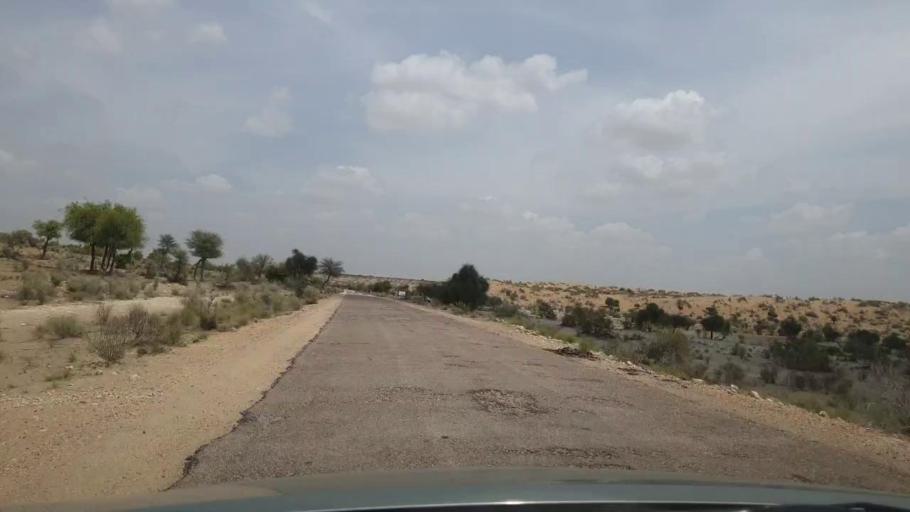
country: PK
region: Sindh
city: Kot Diji
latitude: 27.1751
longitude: 69.1905
